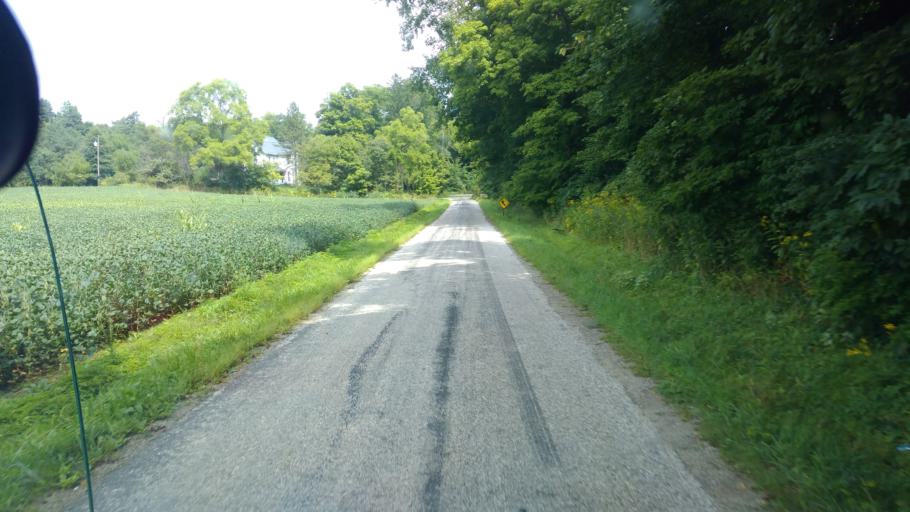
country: US
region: Ohio
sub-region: Ashland County
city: Ashland
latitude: 40.8375
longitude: -82.3812
